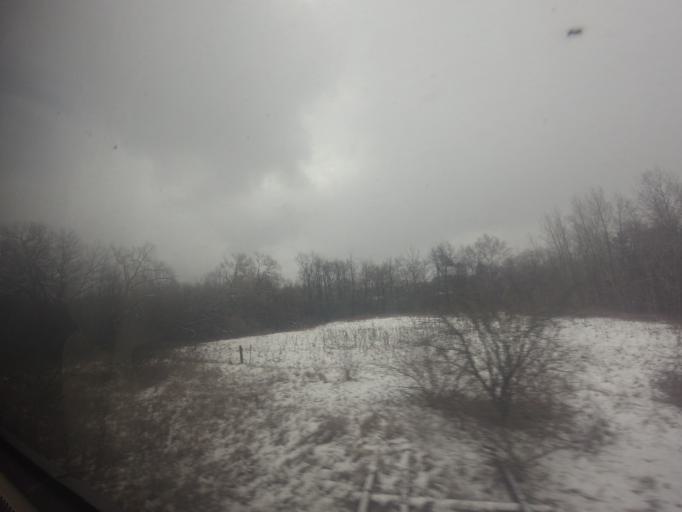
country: CA
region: Ontario
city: Cobourg
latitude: 43.9280
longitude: -78.4161
